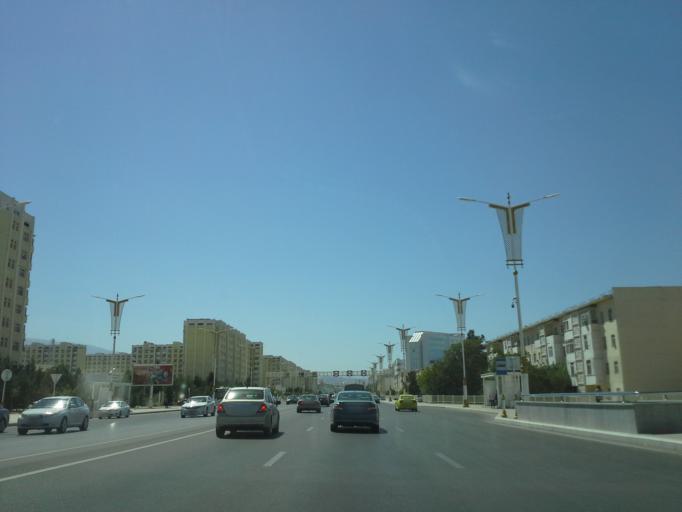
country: TM
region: Ahal
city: Ashgabat
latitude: 37.9103
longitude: 58.4032
